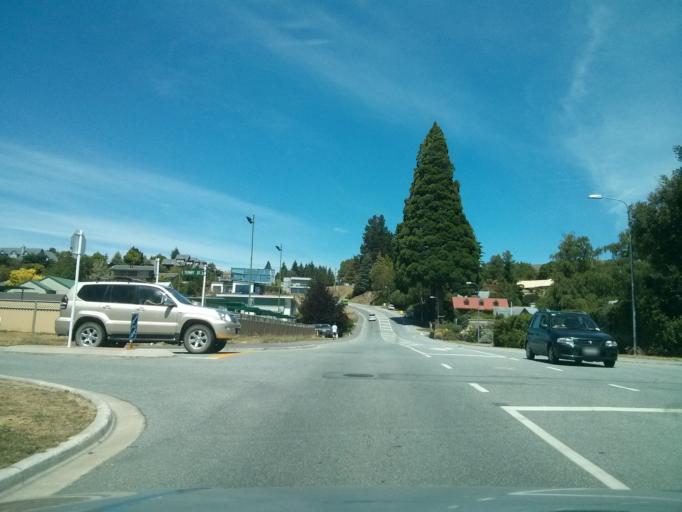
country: NZ
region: Otago
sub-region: Queenstown-Lakes District
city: Wanaka
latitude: -44.7030
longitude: 169.1320
